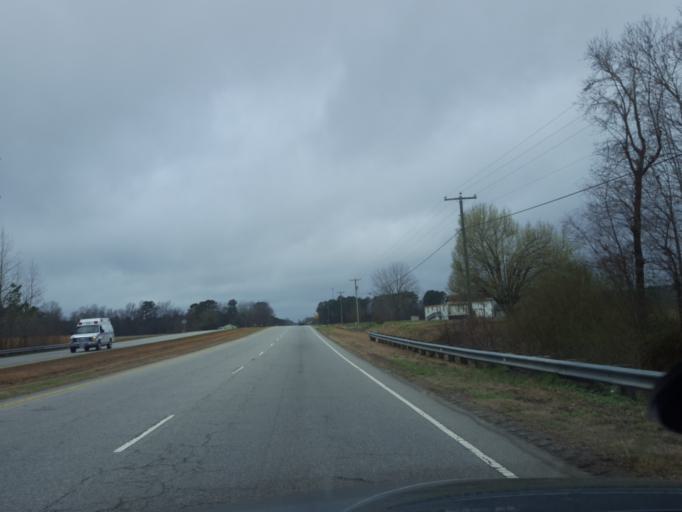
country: US
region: North Carolina
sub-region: Washington County
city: Plymouth
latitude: 35.8130
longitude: -76.8436
